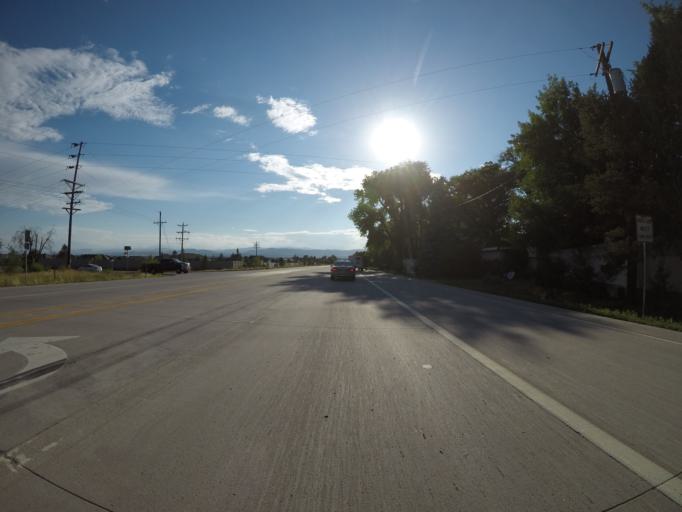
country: US
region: Colorado
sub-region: Larimer County
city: Fort Collins
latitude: 40.5811
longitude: -104.9815
